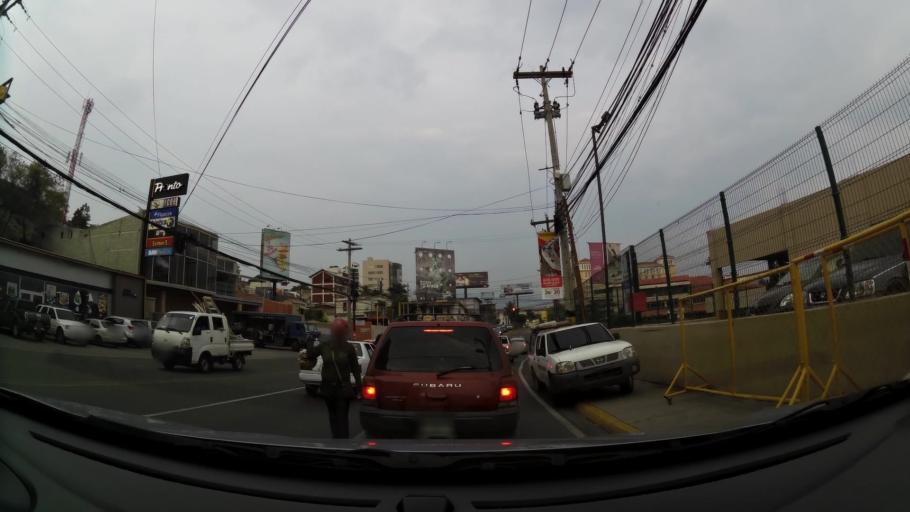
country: HN
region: Francisco Morazan
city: Tegucigalpa
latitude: 14.0894
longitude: -87.1869
